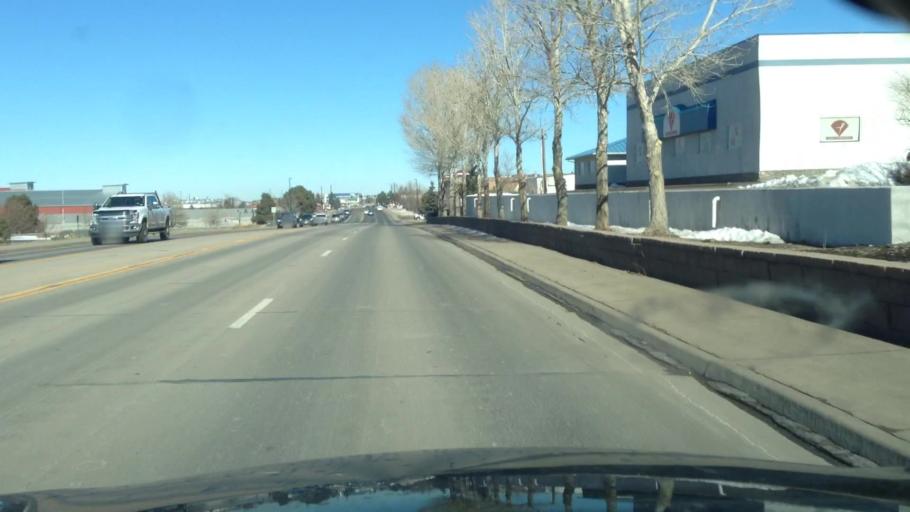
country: US
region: Colorado
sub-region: Douglas County
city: Parker
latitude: 39.5223
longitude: -104.7709
